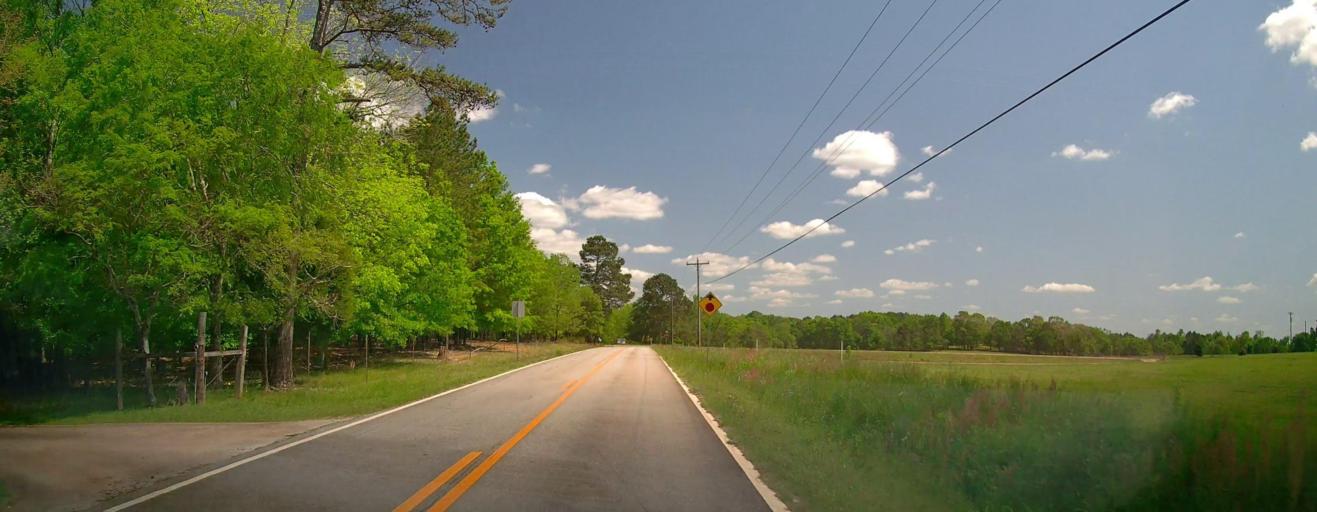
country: US
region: Georgia
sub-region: Putnam County
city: Eatonton
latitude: 33.3233
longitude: -83.3094
